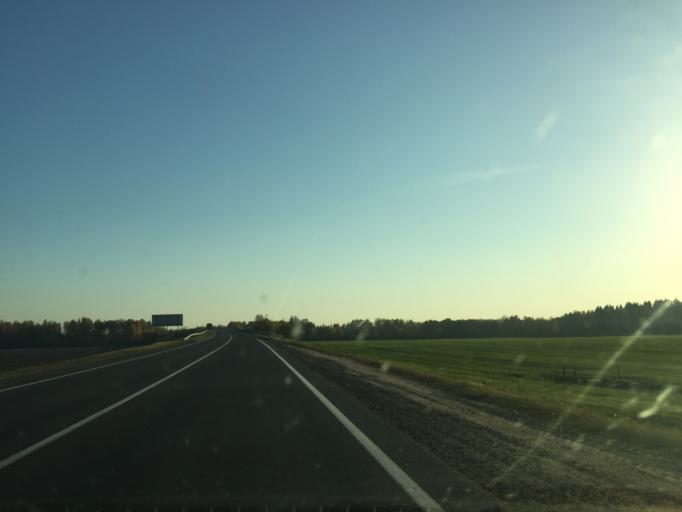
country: BY
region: Mogilev
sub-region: Mahilyowski Rayon
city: Kadino
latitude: 53.8640
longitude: 30.4811
